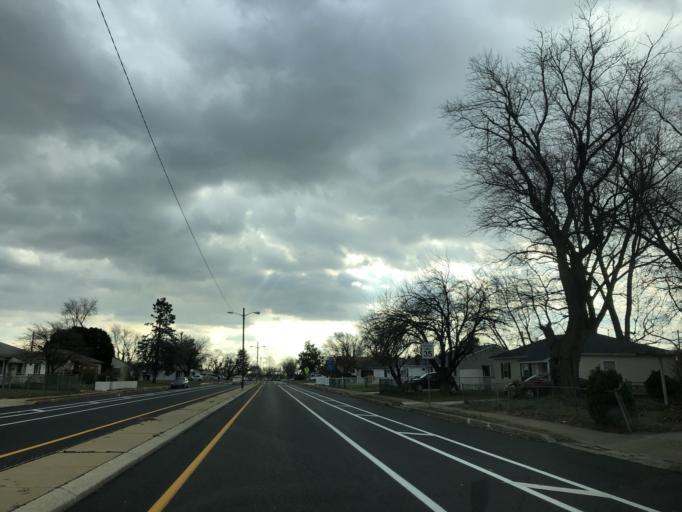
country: US
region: Delaware
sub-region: New Castle County
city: Wilmington Manor
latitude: 39.7052
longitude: -75.5593
